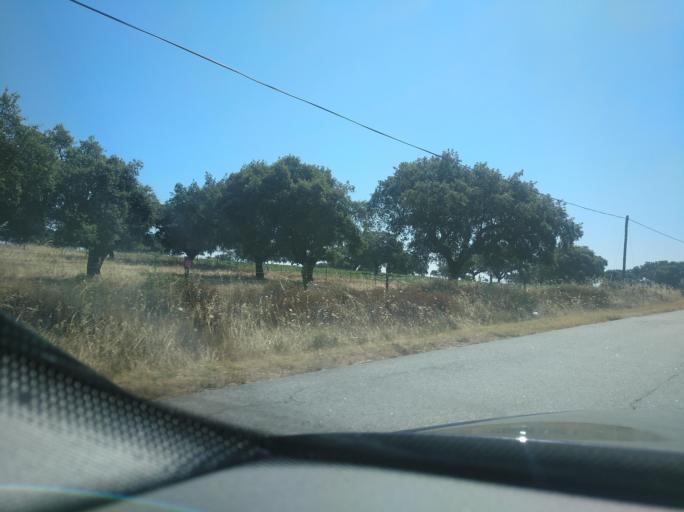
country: PT
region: Portalegre
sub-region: Arronches
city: Arronches
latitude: 38.9938
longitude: -7.3444
